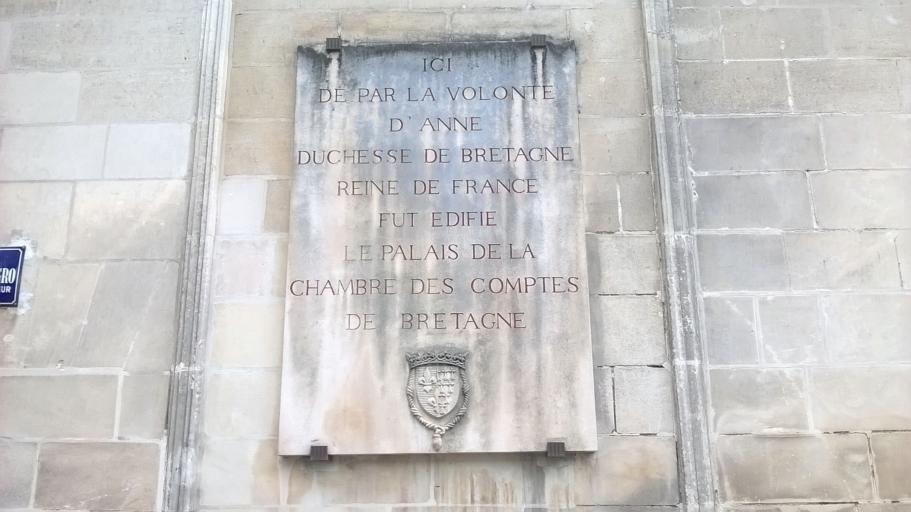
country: FR
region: Pays de la Loire
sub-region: Departement de la Loire-Atlantique
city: Nantes
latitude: 47.2201
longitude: -1.5532
